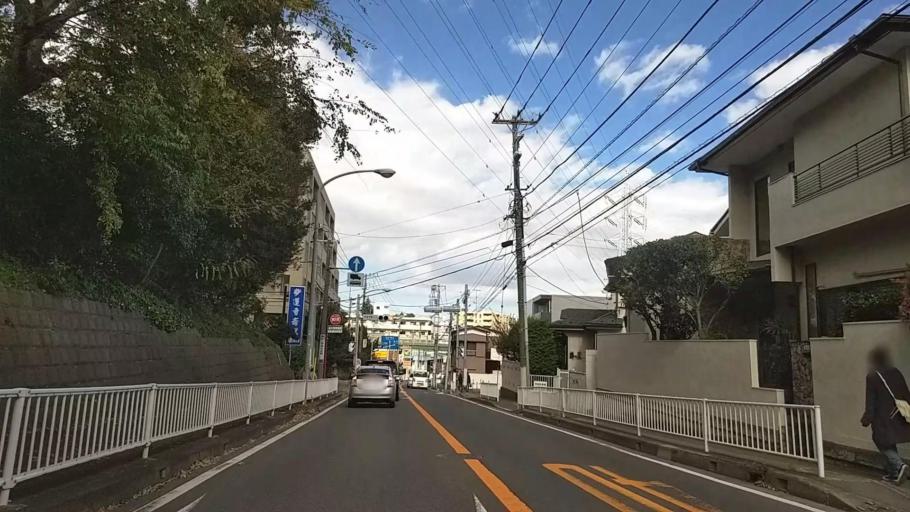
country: JP
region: Kanagawa
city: Yokohama
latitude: 35.4995
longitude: 139.6367
